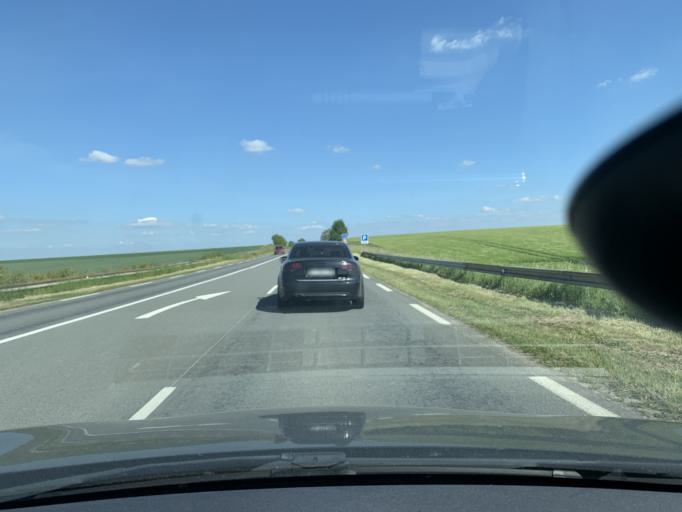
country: FR
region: Nord-Pas-de-Calais
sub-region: Departement du Nord
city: Caudry
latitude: 50.1281
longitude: 3.4374
